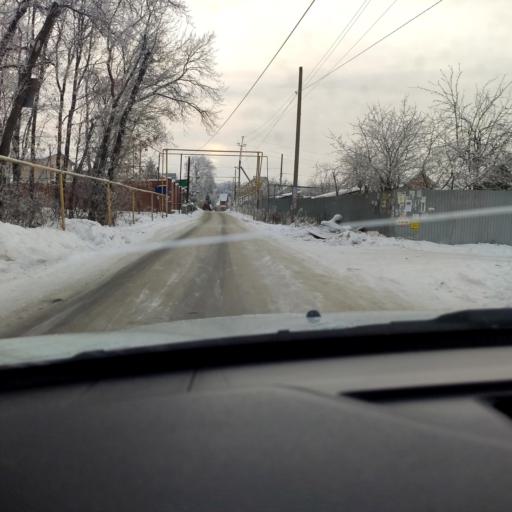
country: RU
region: Samara
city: Petra-Dubrava
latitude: 53.2981
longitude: 50.2489
